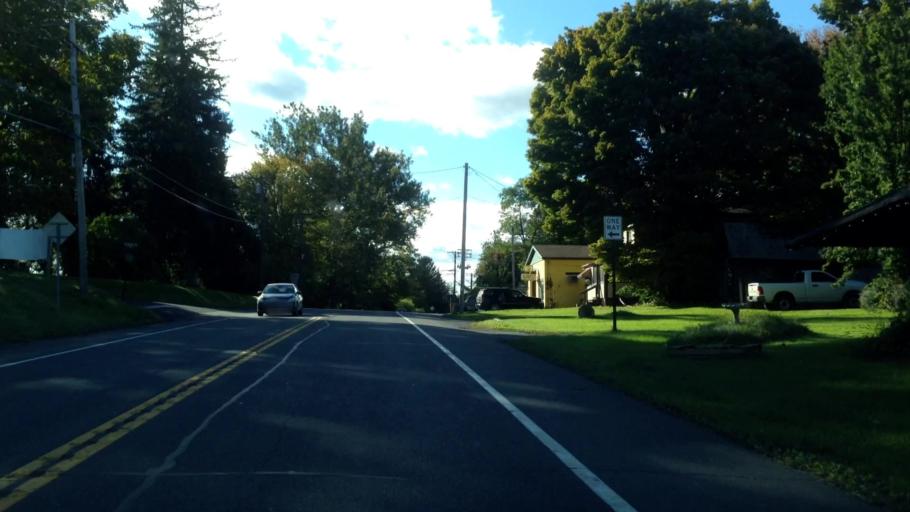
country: US
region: New York
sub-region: Ulster County
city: Port Ewen
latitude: 41.8571
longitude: -73.9702
